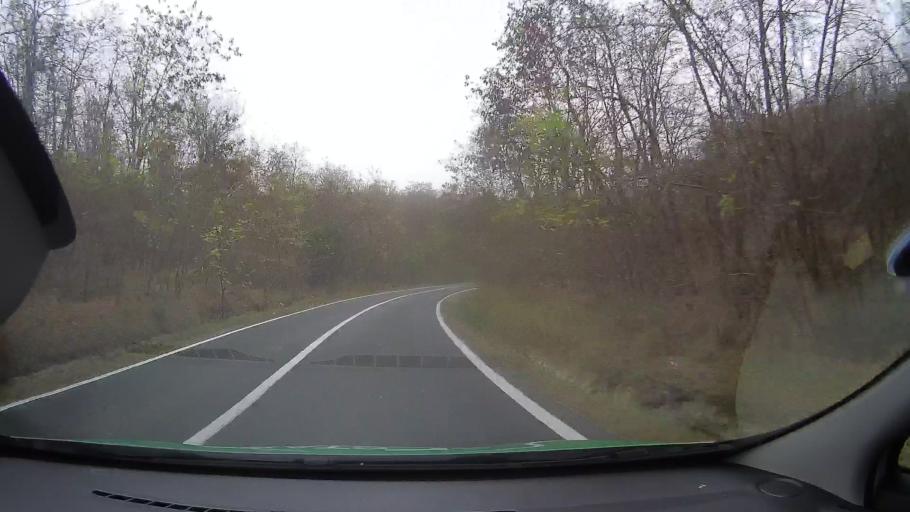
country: RO
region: Constanta
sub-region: Comuna Garliciu
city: Garliciu
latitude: 44.7076
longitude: 28.0750
